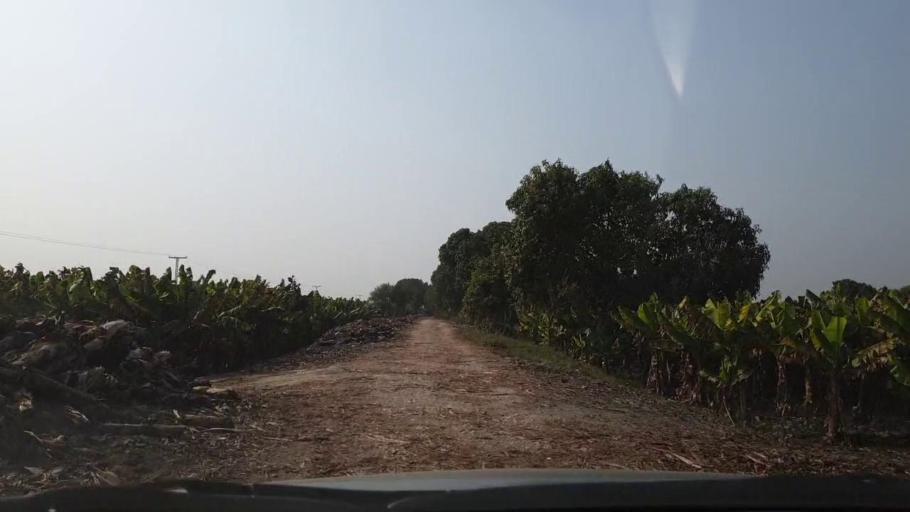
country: PK
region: Sindh
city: Matiari
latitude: 25.6329
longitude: 68.5673
